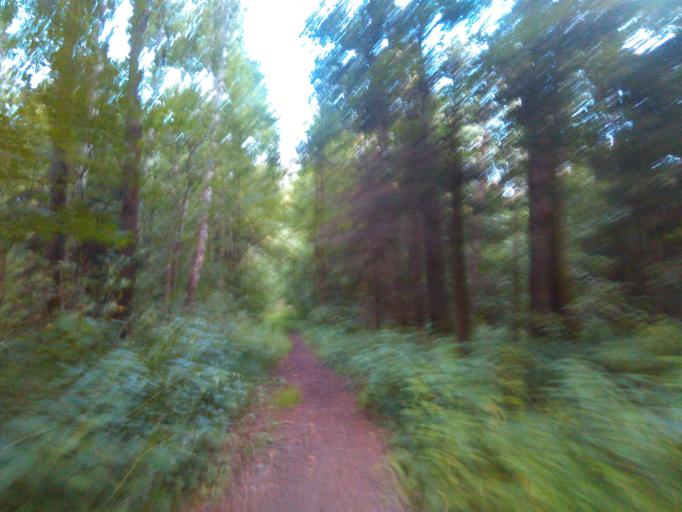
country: RU
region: Moskovskaya
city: Bogorodskoye
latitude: 55.8373
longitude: 37.7208
